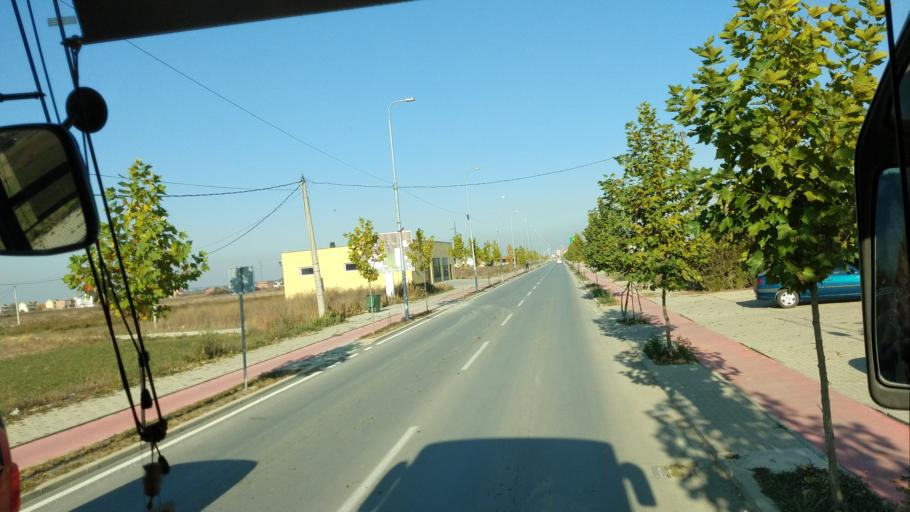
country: XK
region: Ferizaj
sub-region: Komuna e Shtimes
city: Shtime
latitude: 42.4397
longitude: 21.0512
